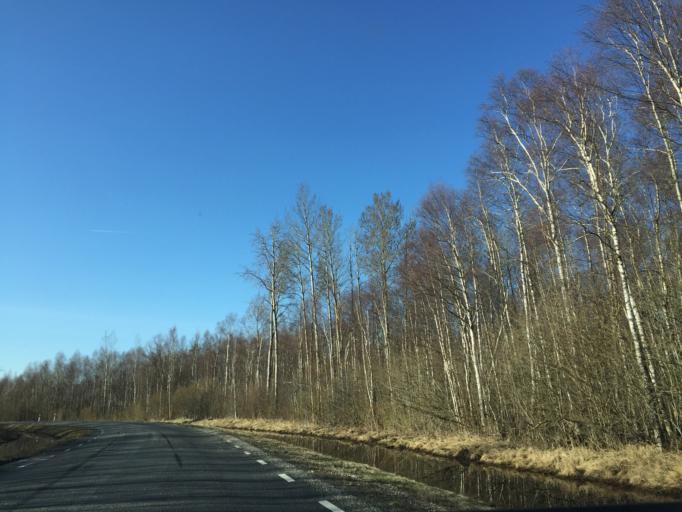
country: RU
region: Pskov
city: Gdov
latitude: 59.0050
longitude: 27.6928
